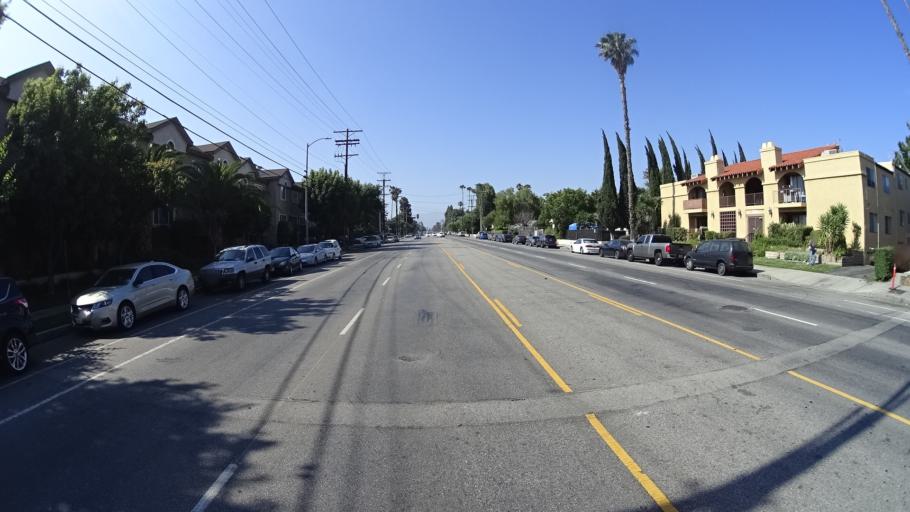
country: US
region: California
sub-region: Los Angeles County
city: Van Nuys
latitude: 34.1889
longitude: -118.4313
